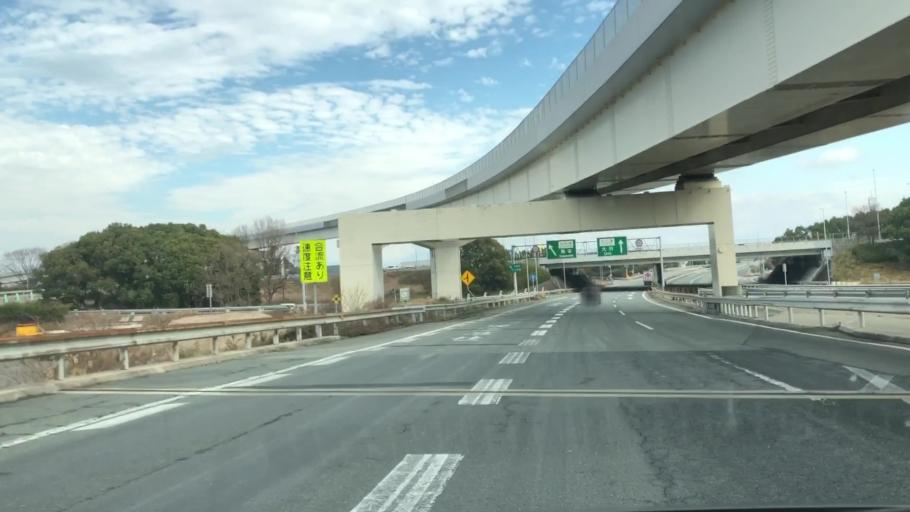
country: JP
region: Saga Prefecture
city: Tosu
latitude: 33.3962
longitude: 130.5365
